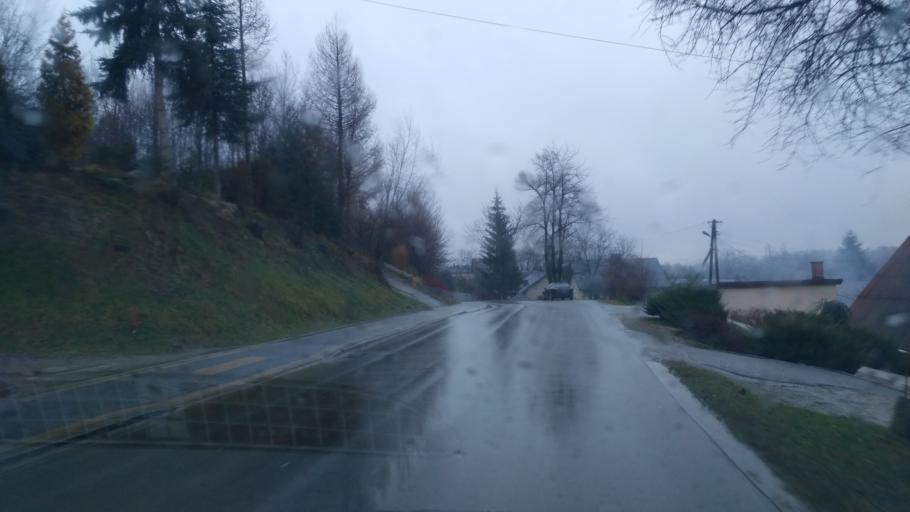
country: PL
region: Subcarpathian Voivodeship
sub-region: Powiat krosnienski
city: Kroscienko Wyzne
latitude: 49.6794
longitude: 21.8279
